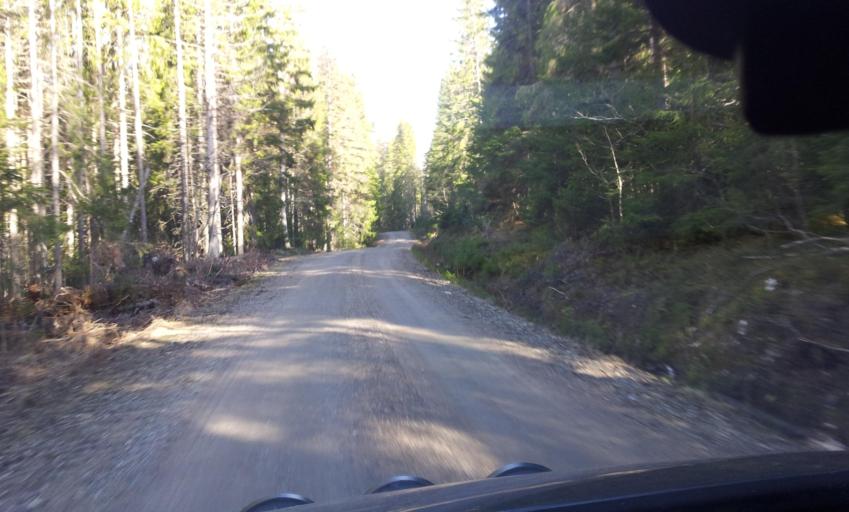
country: SE
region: Vaesternorrland
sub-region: Ange Kommun
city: Ange
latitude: 62.2110
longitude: 15.4212
